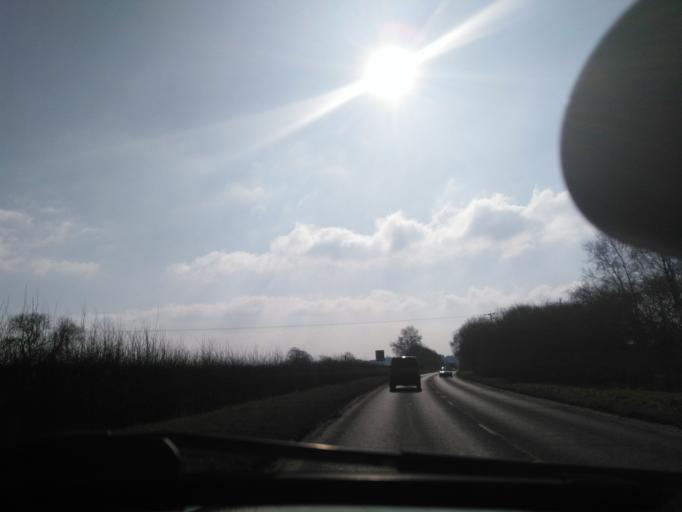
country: GB
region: England
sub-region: Wiltshire
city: Malmesbury
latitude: 51.5889
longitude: -2.0884
